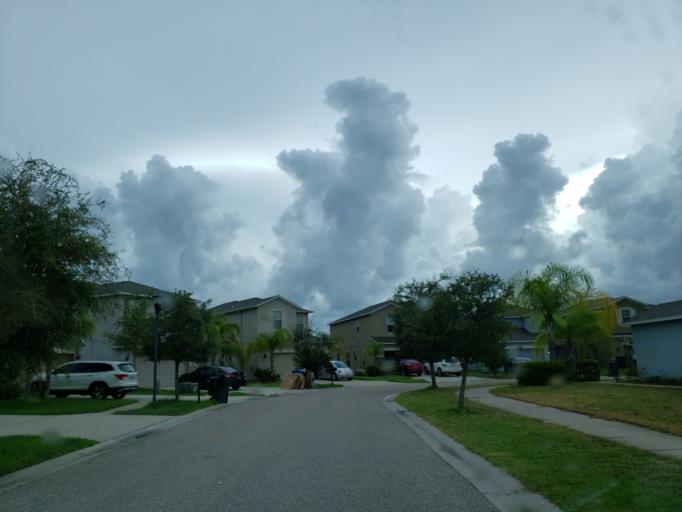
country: US
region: Florida
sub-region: Hillsborough County
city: Ruskin
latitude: 27.7292
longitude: -82.4044
